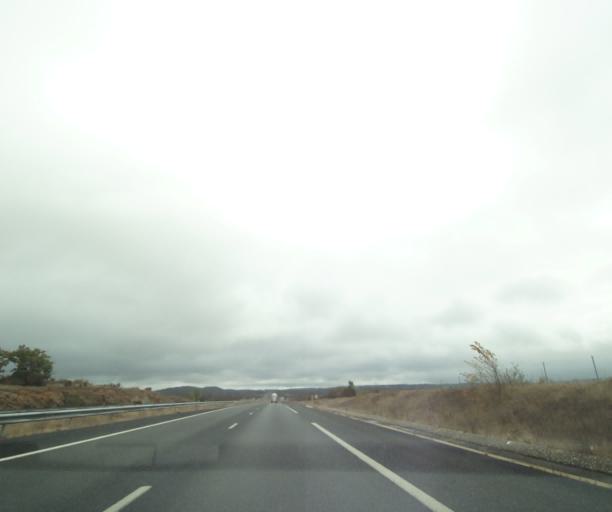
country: FR
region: Midi-Pyrenees
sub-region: Departement de l'Aveyron
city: La Cavalerie
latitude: 43.9451
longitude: 3.2212
